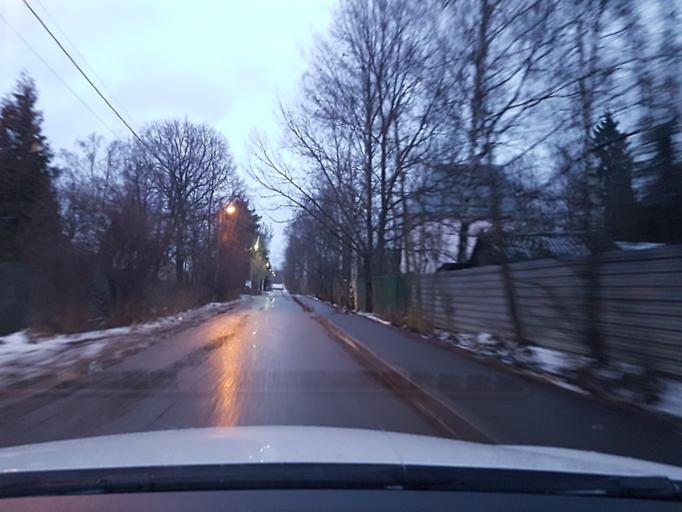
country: RU
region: Moskovskaya
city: Sheremet'yevskiy
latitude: 55.9837
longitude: 37.5018
